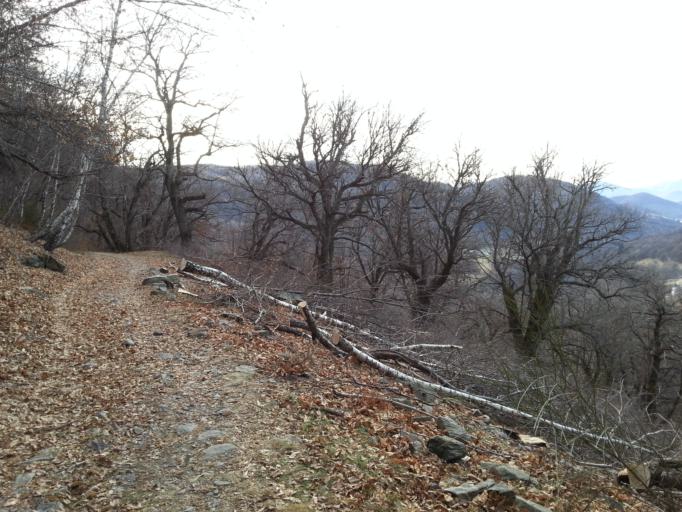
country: CH
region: Ticino
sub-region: Lugano District
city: Gravesano
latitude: 46.0525
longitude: 8.8882
